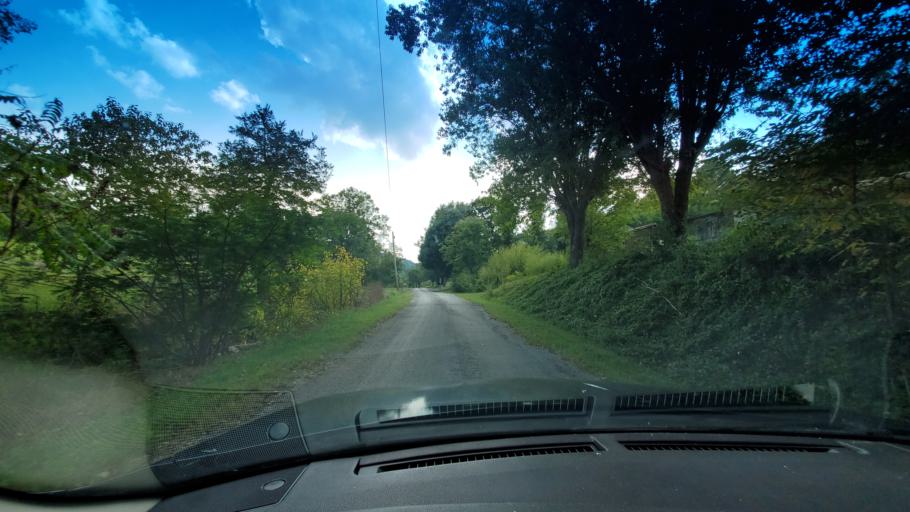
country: US
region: Tennessee
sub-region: Smith County
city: South Carthage
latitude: 36.2296
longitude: -85.9806
